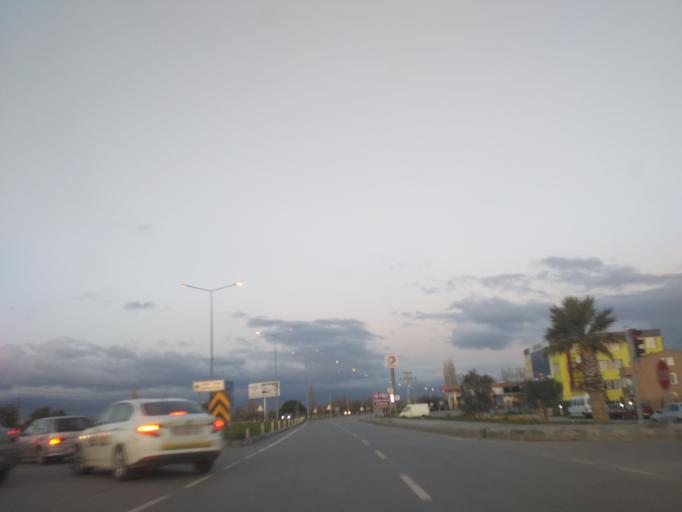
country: TR
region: Balikesir
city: Burhaniye
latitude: 39.5126
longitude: 26.9763
